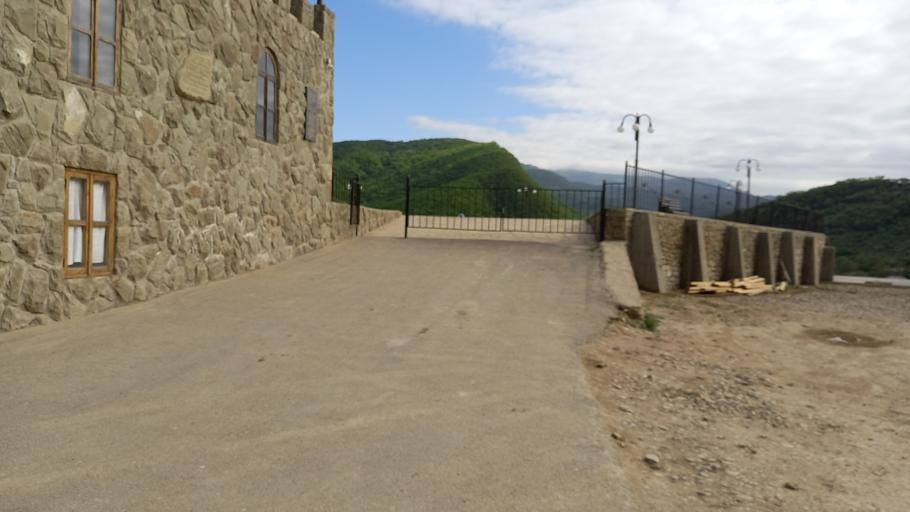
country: RU
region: Dagestan
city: Khuchni
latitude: 41.9651
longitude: 47.9565
